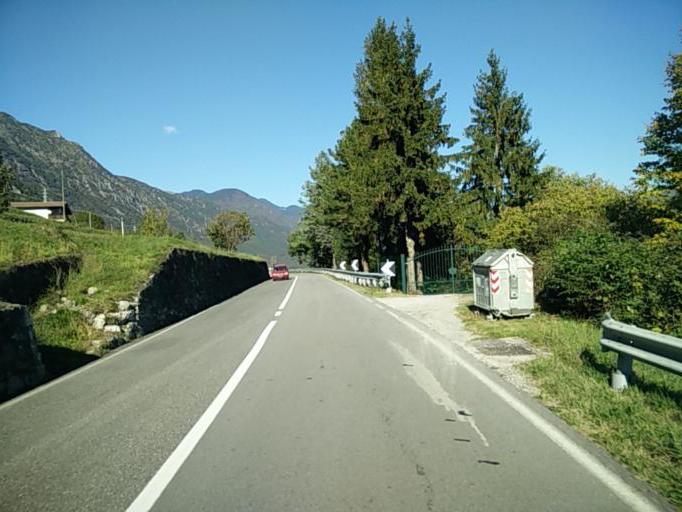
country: IT
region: Lombardy
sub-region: Provincia di Brescia
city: Anfo
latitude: 45.7847
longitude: 10.5007
